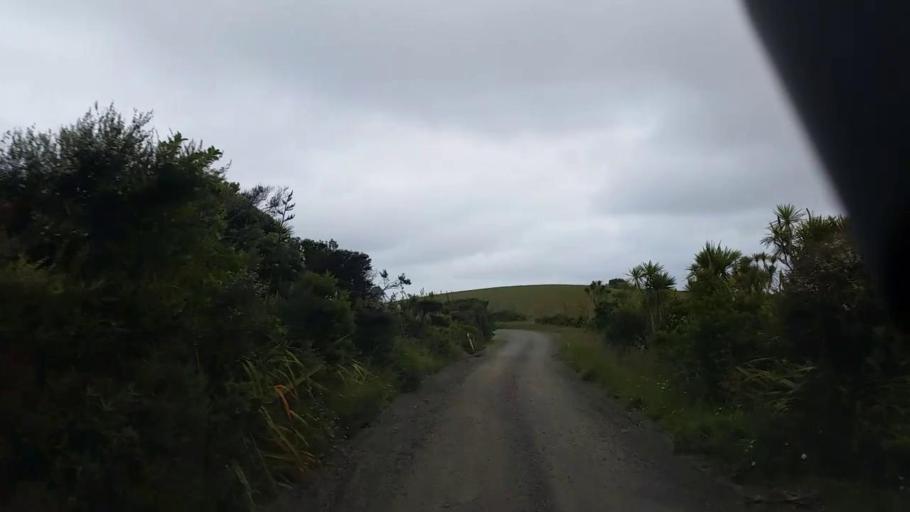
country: NZ
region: Auckland
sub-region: Auckland
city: Muriwai Beach
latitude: -36.9318
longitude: 174.4635
